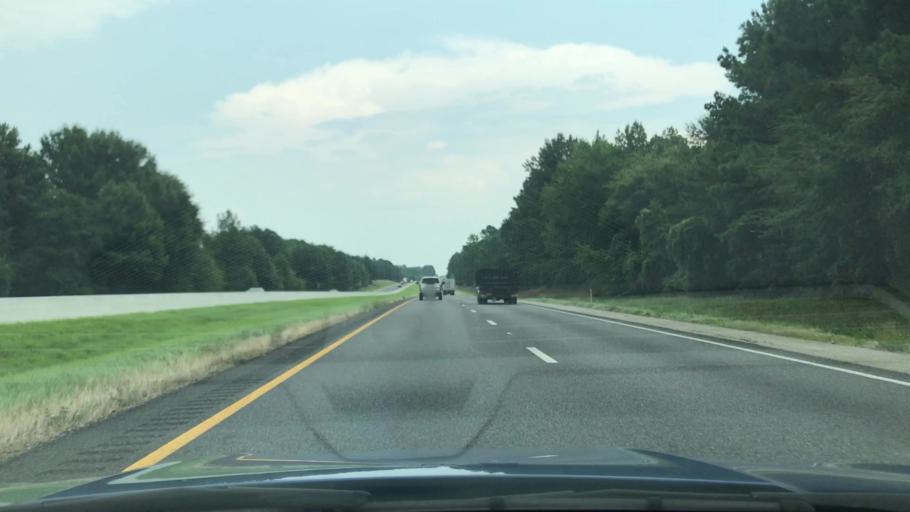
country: US
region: Texas
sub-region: Gregg County
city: Liberty City
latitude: 32.4357
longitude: -94.9707
